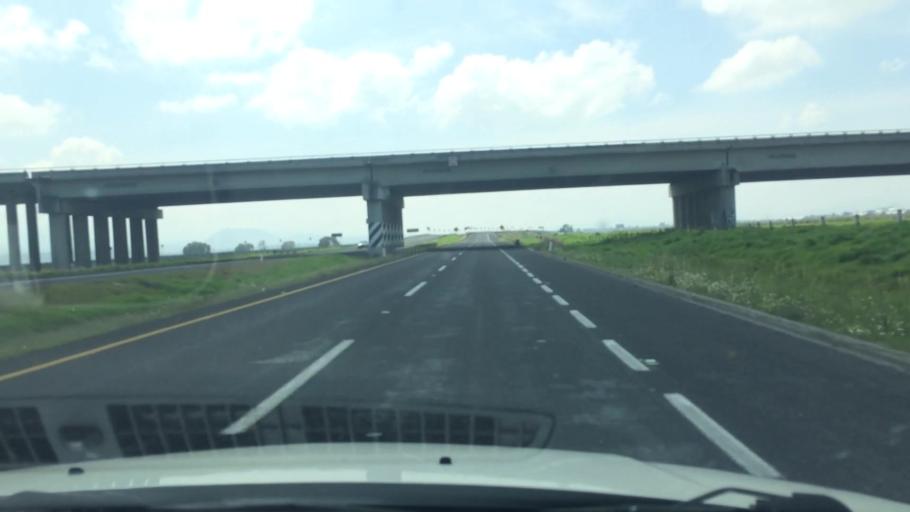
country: MX
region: Mexico
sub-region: Toluca
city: El Cerrillo Vista Hermosa
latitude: 19.3236
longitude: -99.5228
